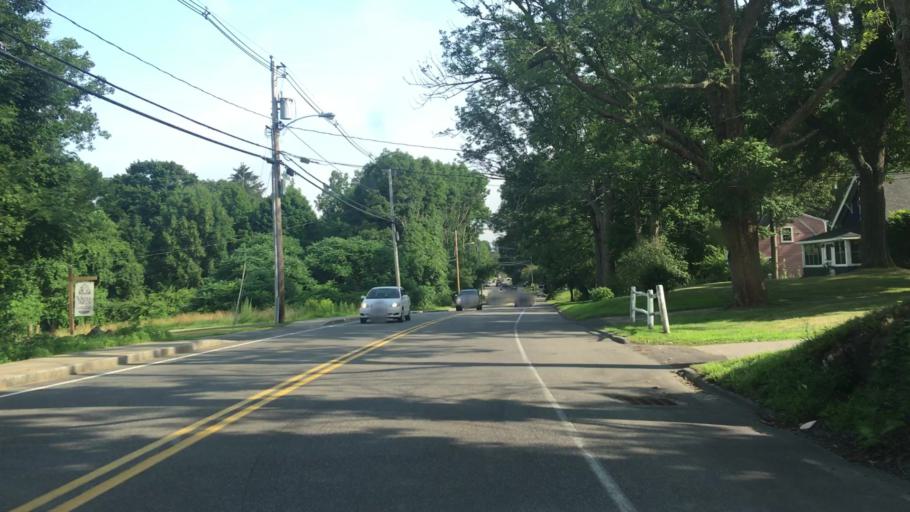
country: US
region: Maine
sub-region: York County
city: Kittery
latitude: 43.0966
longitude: -70.7382
